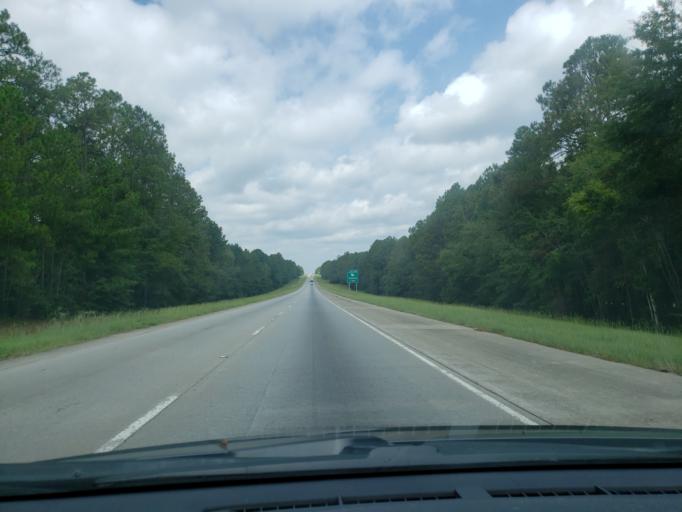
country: US
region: Georgia
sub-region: Emanuel County
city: Swainsboro
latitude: 32.4129
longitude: -82.3686
